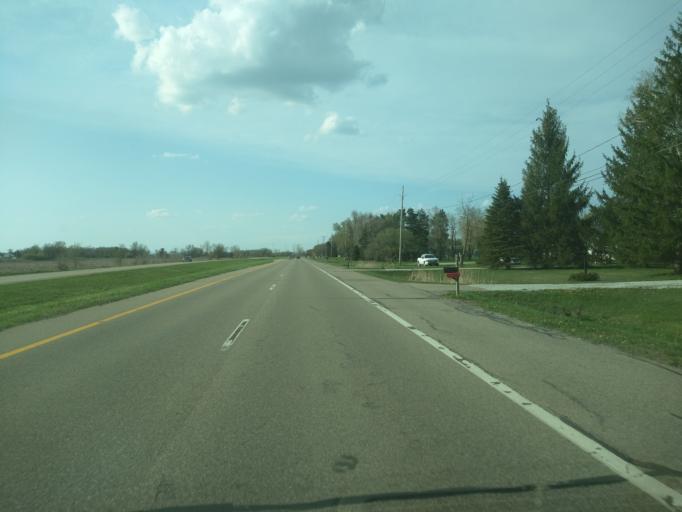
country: US
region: Michigan
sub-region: Eaton County
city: Dimondale
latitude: 42.6341
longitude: -84.6228
